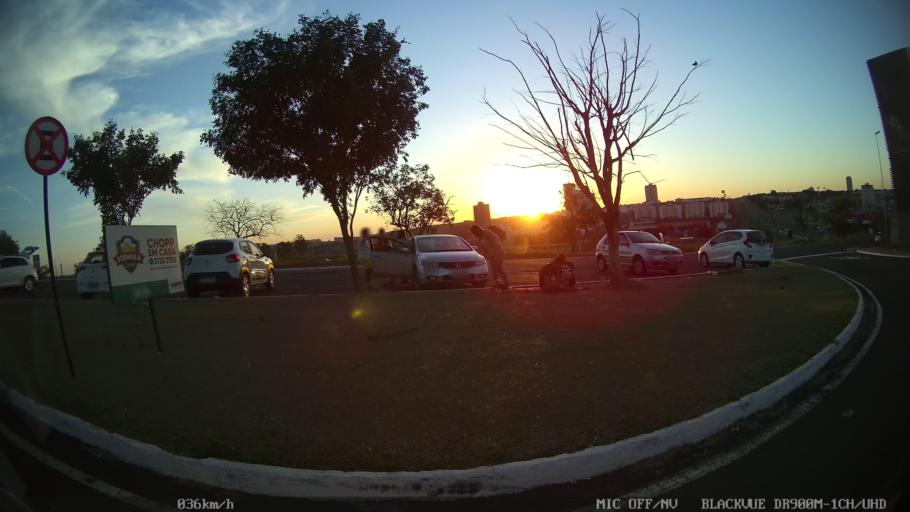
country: BR
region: Sao Paulo
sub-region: Franca
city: Franca
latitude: -20.5570
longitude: -47.4080
